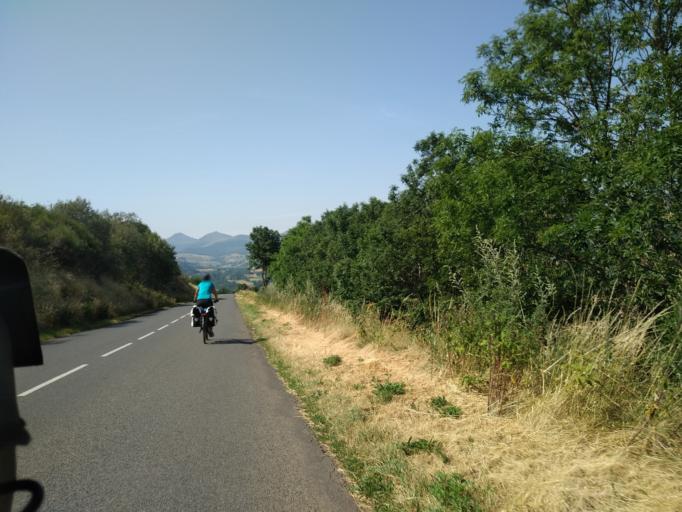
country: FR
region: Auvergne
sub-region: Departement du Cantal
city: Riom-es-Montagnes
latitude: 45.2215
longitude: 2.7214
